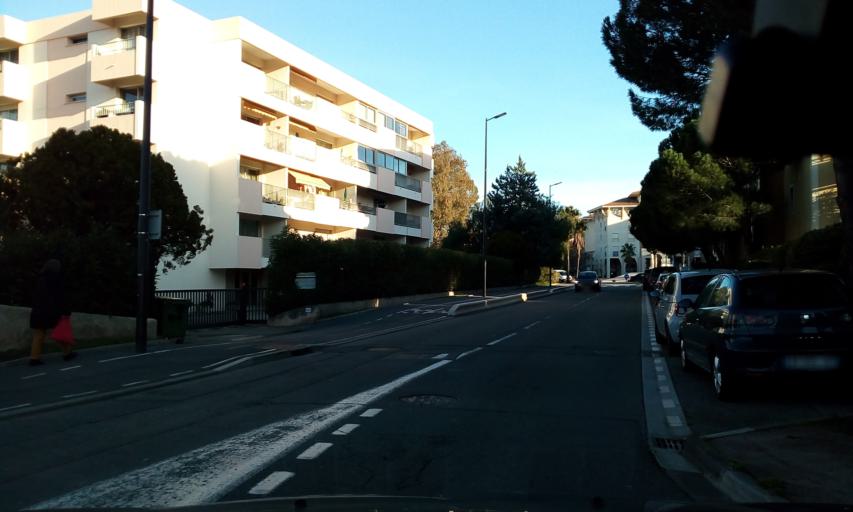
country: FR
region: Provence-Alpes-Cote d'Azur
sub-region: Departement du Var
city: Frejus
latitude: 43.4249
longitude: 6.7464
